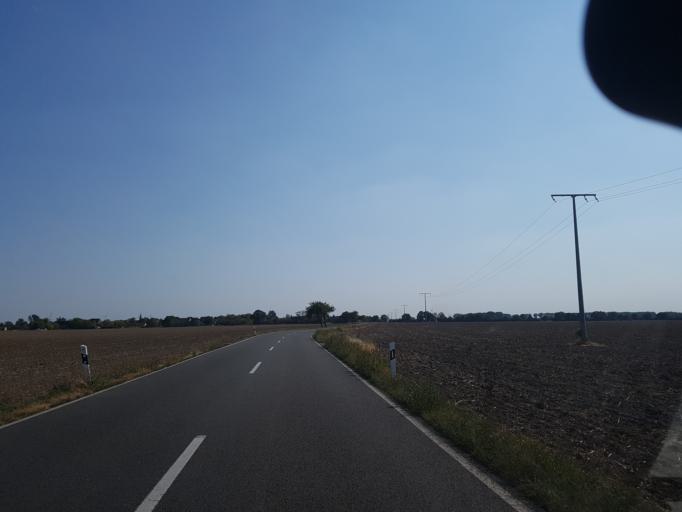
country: DE
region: Saxony-Anhalt
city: Annaburg
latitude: 51.6830
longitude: 12.9964
